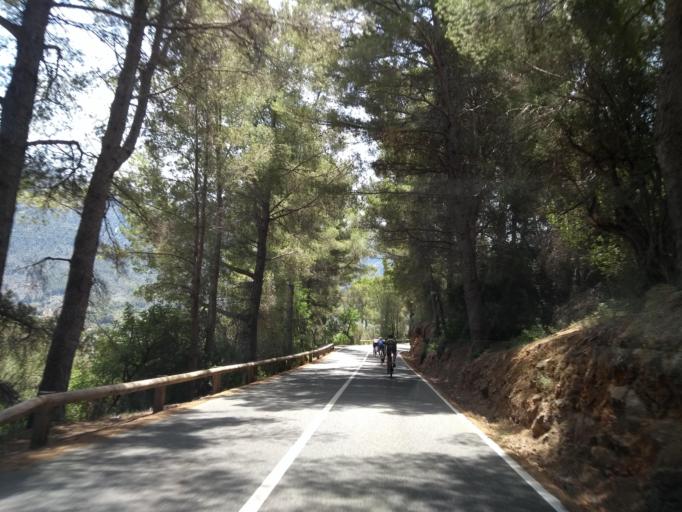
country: ES
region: Balearic Islands
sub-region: Illes Balears
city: Soller
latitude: 39.7803
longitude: 2.7236
